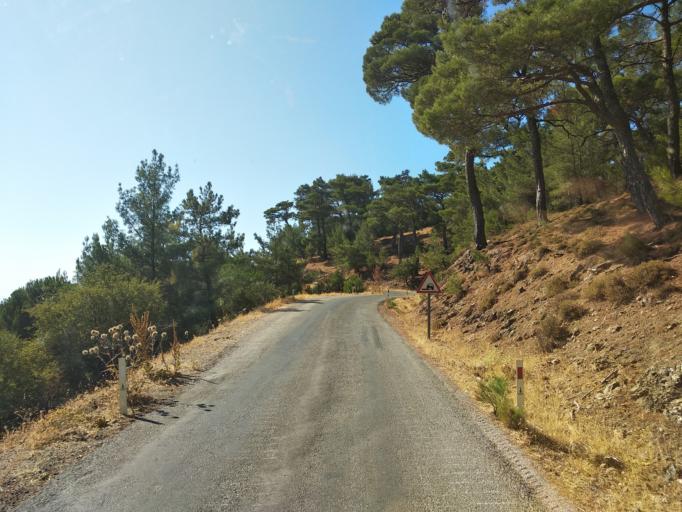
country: TR
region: Izmir
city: Gaziemir
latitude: 38.2984
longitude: 26.9977
